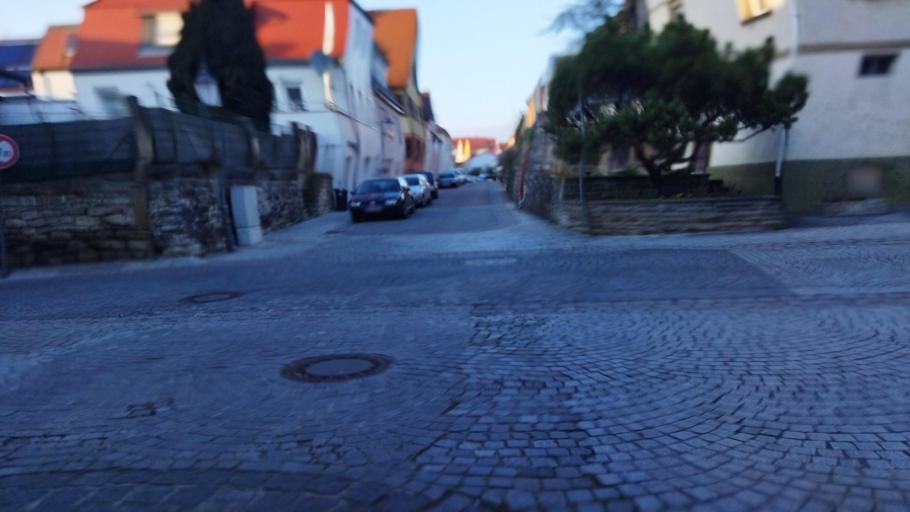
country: DE
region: Baden-Wuerttemberg
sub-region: Regierungsbezirk Stuttgart
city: Gemmrigheim
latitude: 49.0252
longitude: 9.1571
